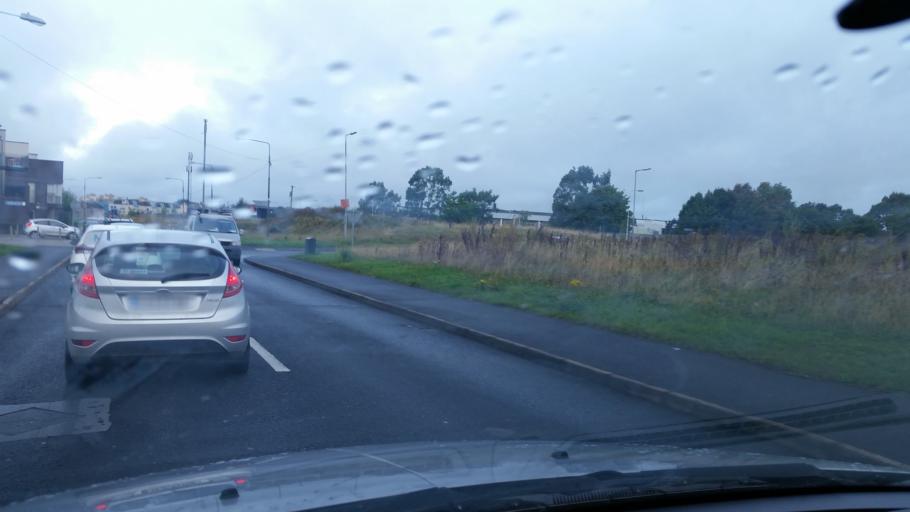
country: IE
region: Leinster
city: Ballymun
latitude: 53.4015
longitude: -6.2682
